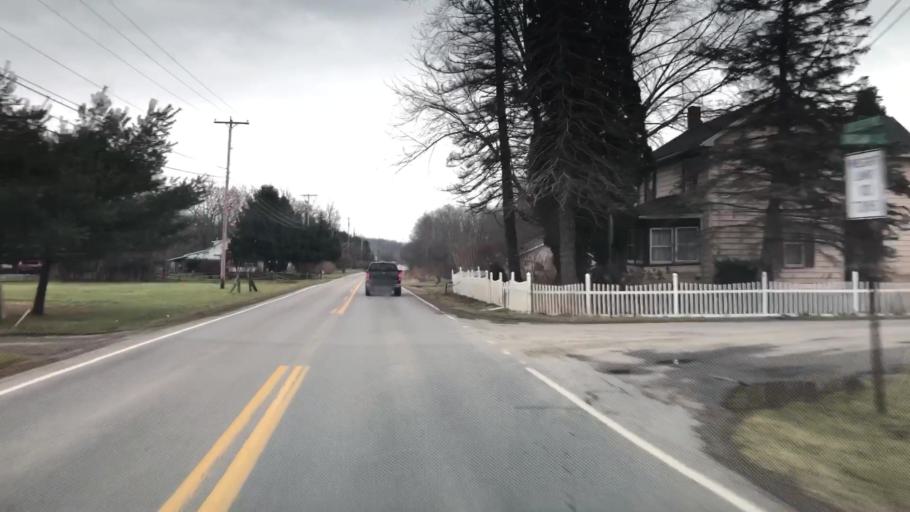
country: US
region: Pennsylvania
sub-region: Mercer County
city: Grove City
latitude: 41.1414
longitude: -80.1449
